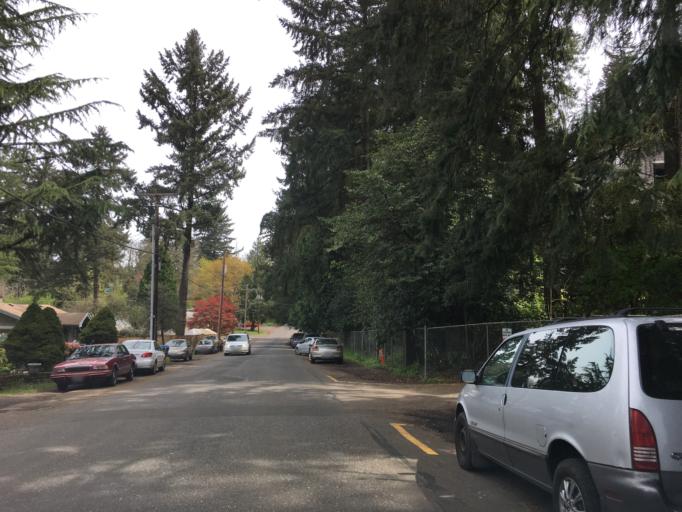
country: US
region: Oregon
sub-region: Multnomah County
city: Lents
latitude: 45.5536
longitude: -122.5719
